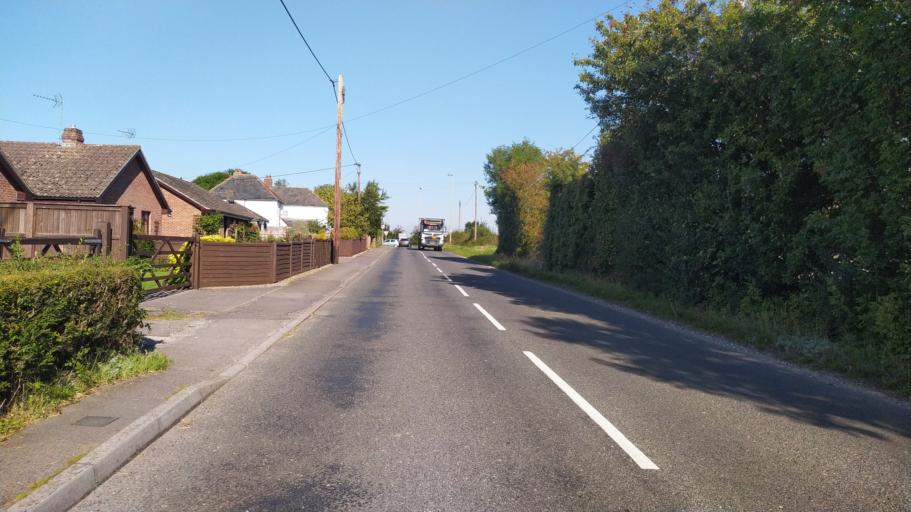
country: GB
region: England
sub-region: Hampshire
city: Abbotts Ann
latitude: 51.1583
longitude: -1.5605
